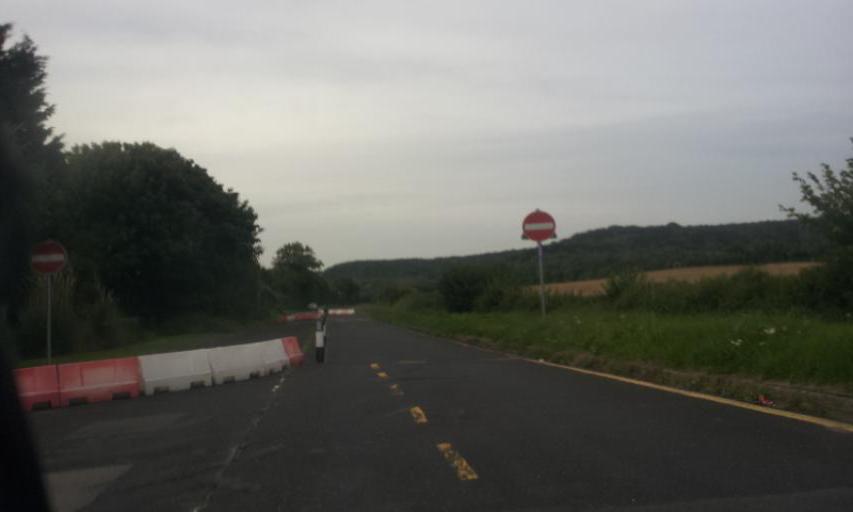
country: GB
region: England
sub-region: Kent
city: Boxley
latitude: 51.3083
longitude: 0.5142
